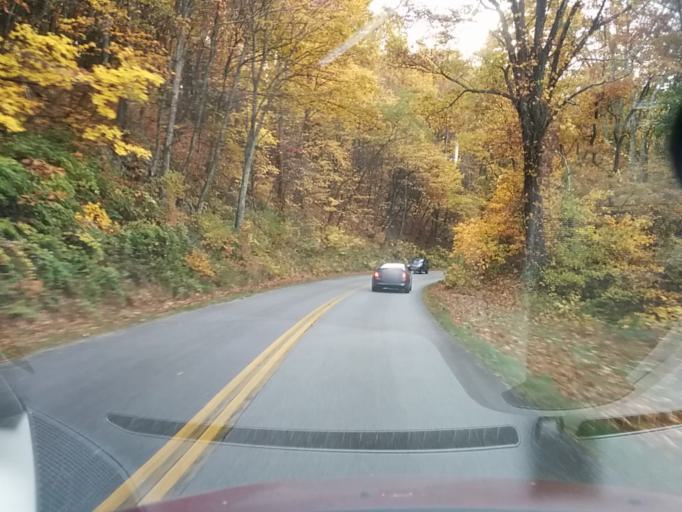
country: US
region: Virginia
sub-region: City of Buena Vista
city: Buena Vista
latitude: 37.8095
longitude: -79.2383
